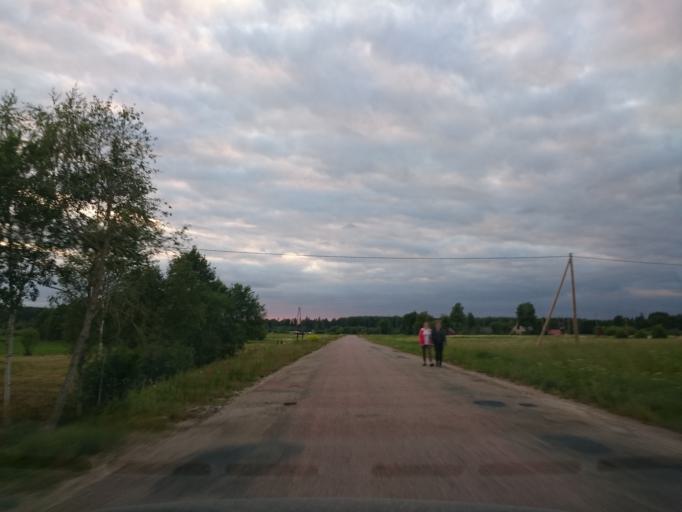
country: LV
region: Ropazu
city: Ropazi
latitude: 56.9644
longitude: 24.6833
